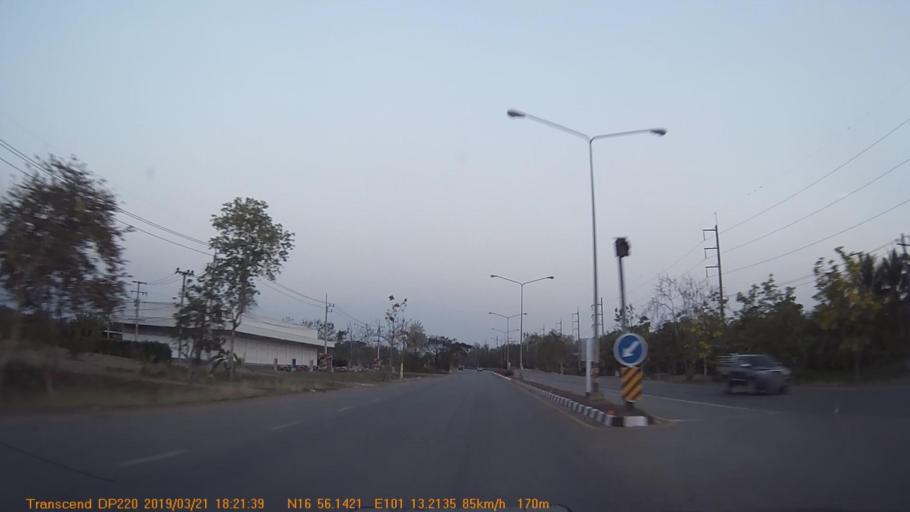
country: TH
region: Phetchabun
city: Lom Kao
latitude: 16.9353
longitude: 101.2204
